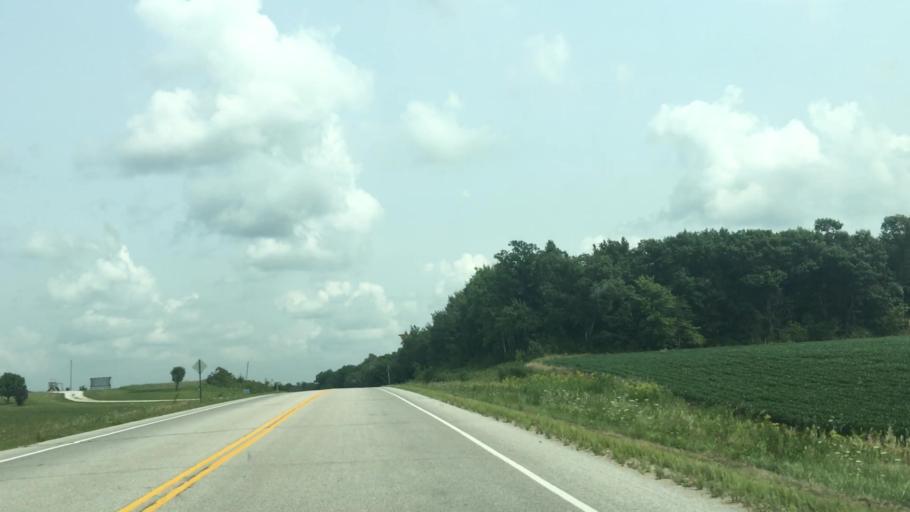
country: US
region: Minnesota
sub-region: Fillmore County
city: Harmony
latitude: 43.6428
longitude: -91.9286
